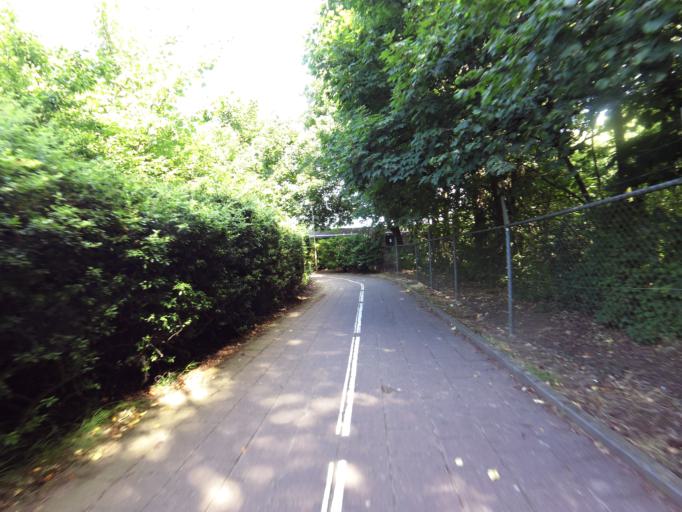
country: NL
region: Limburg
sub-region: Gemeente Heerlen
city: Heerlen
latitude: 50.9006
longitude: 6.0270
